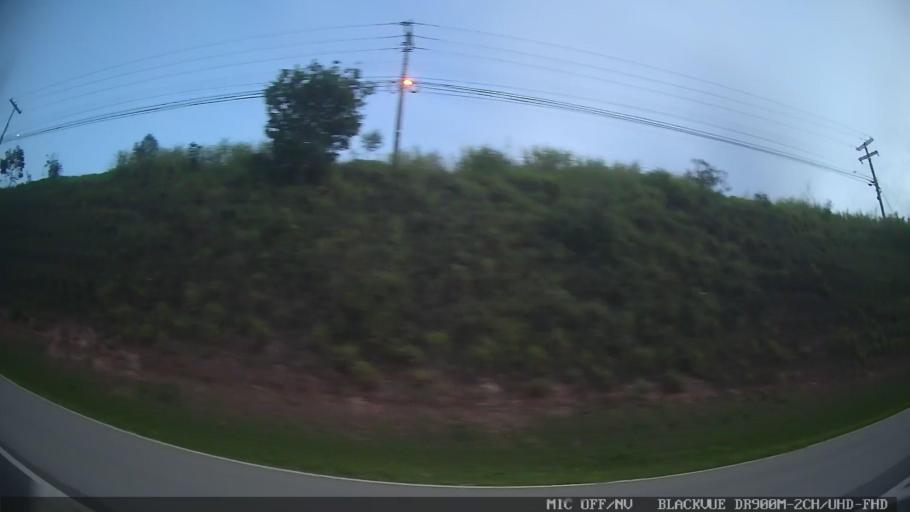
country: BR
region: Sao Paulo
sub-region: Cabreuva
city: Cabreuva
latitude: -23.2570
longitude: -47.1035
